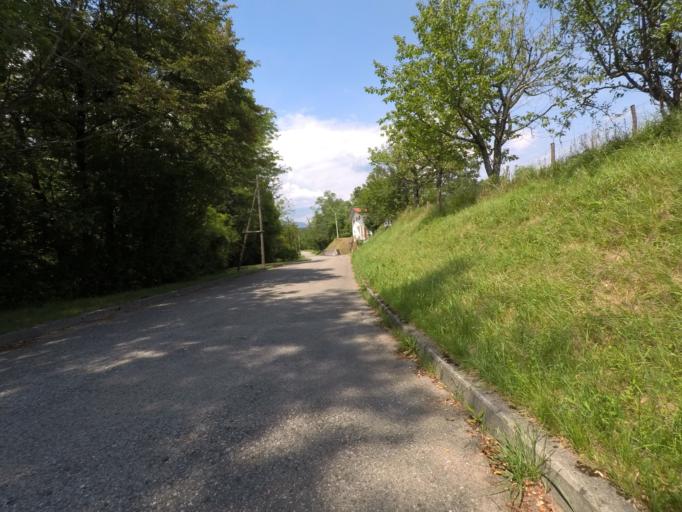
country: IT
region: Friuli Venezia Giulia
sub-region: Provincia di Pordenone
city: Lestans
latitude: 46.1796
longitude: 12.8935
